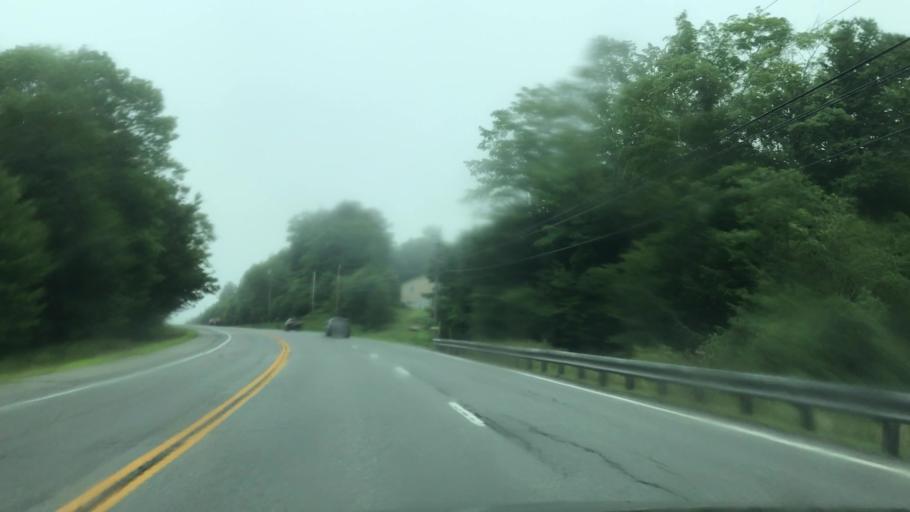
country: US
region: Maine
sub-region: Lincoln County
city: Waldoboro
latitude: 44.1000
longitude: -69.4214
